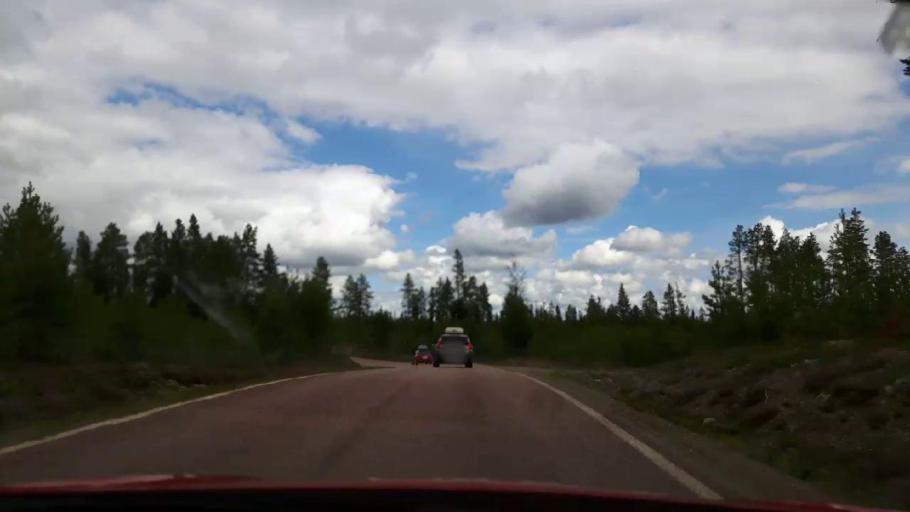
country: NO
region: Hedmark
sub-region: Trysil
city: Innbygda
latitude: 61.8696
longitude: 12.9591
